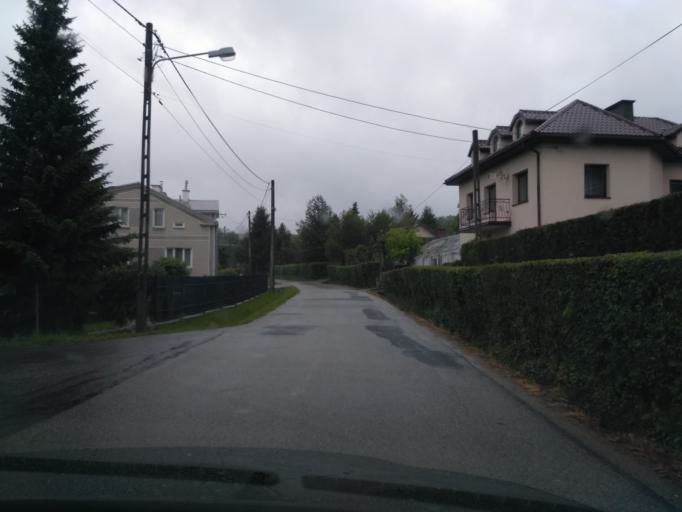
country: PL
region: Lesser Poland Voivodeship
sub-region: Powiat gorlicki
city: Gorlice
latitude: 49.6684
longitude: 21.1402
